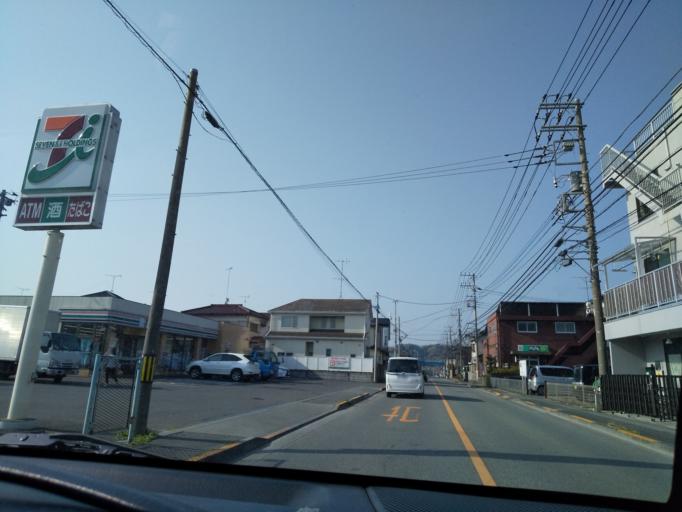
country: JP
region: Tokyo
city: Fussa
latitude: 35.7232
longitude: 139.3185
